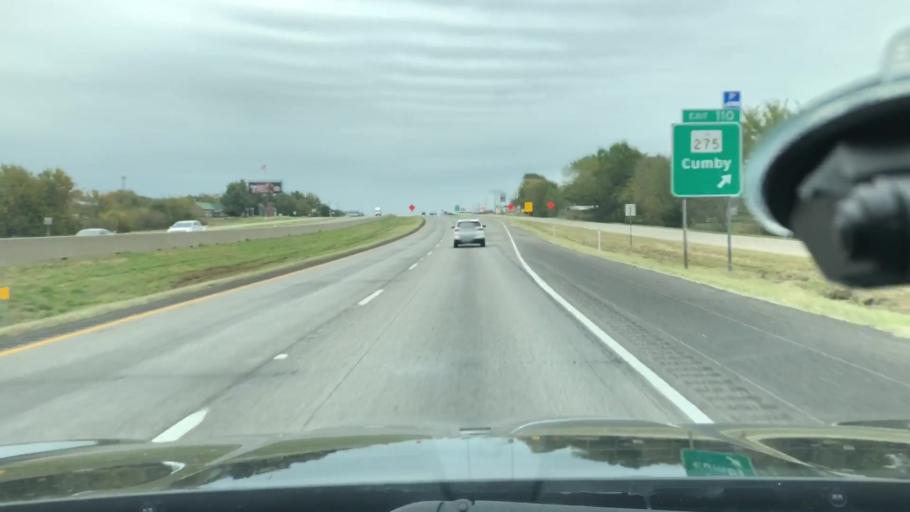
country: US
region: Texas
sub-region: Hunt County
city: Commerce
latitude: 33.1290
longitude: -95.8455
